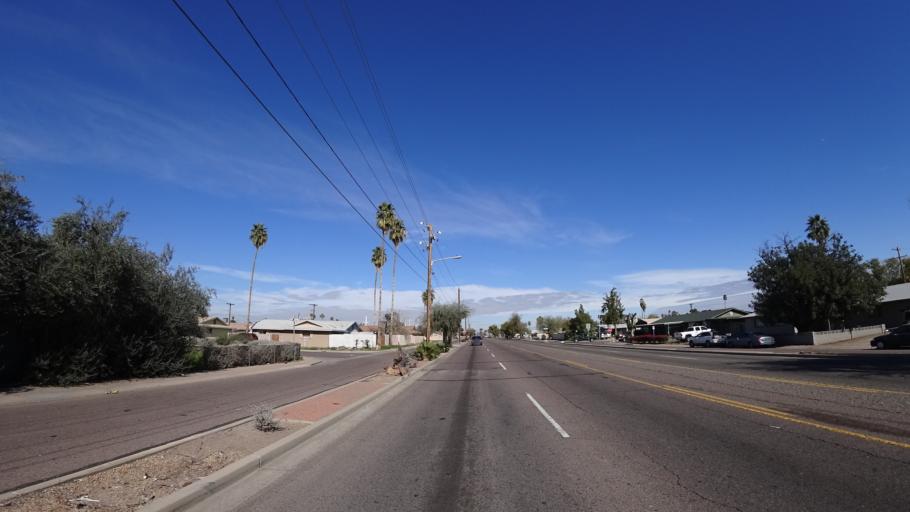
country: US
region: Arizona
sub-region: Maricopa County
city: Glendale
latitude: 33.5052
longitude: -112.1865
